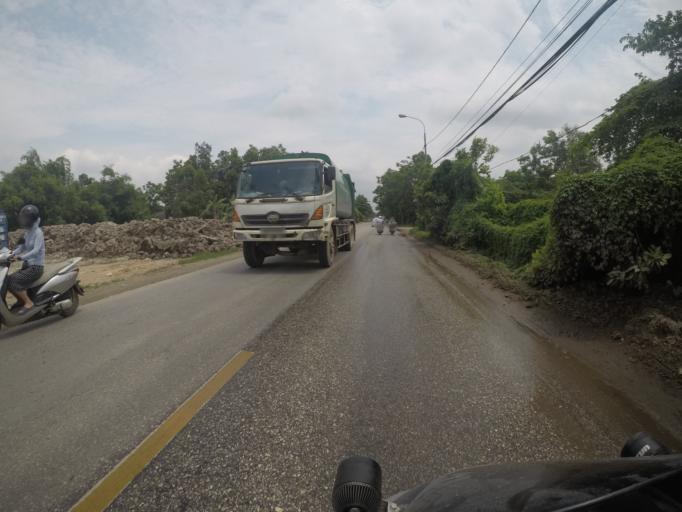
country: VN
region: Ha Noi
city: Soc Son
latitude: 21.2339
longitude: 105.8492
